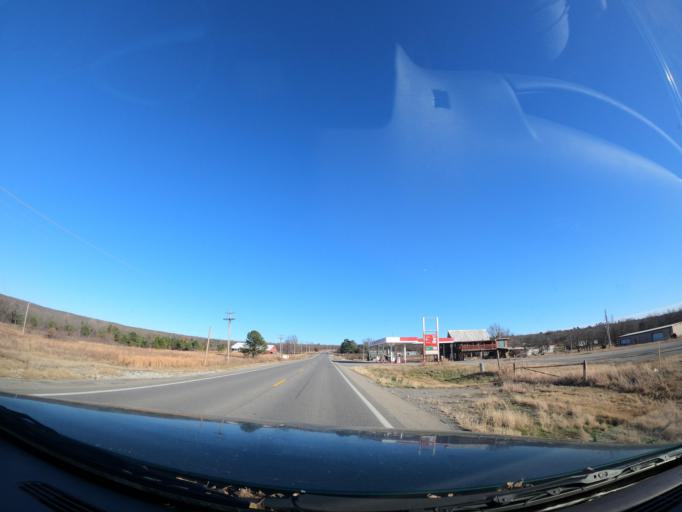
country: US
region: Oklahoma
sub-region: Pittsburg County
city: Longtown
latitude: 35.2392
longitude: -95.4809
